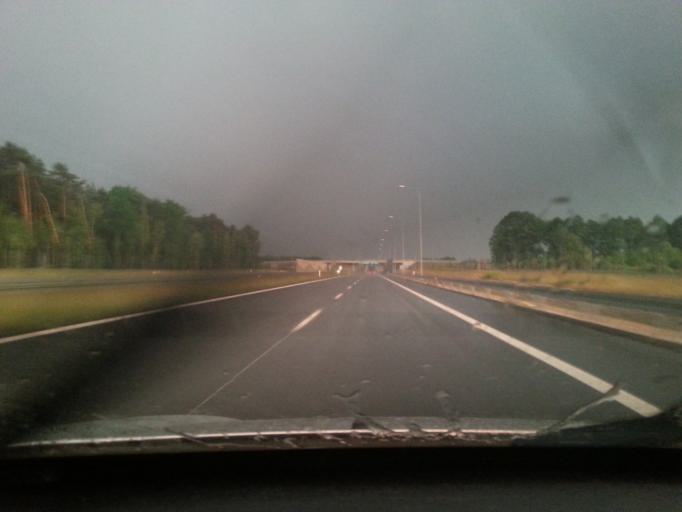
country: PL
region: Lodz Voivodeship
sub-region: Powiat pabianicki
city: Dobron
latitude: 51.6094
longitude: 19.2747
